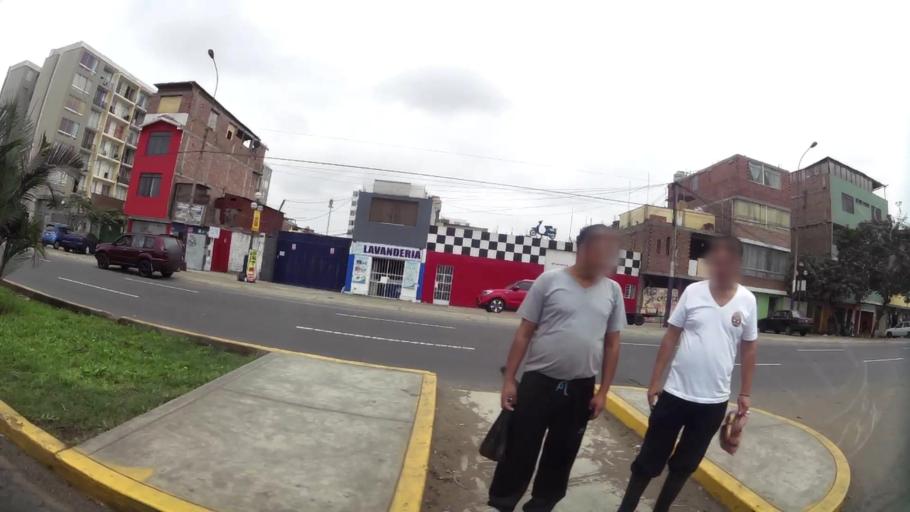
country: PE
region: Lima
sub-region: Lima
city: Surco
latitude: -12.1763
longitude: -76.9947
